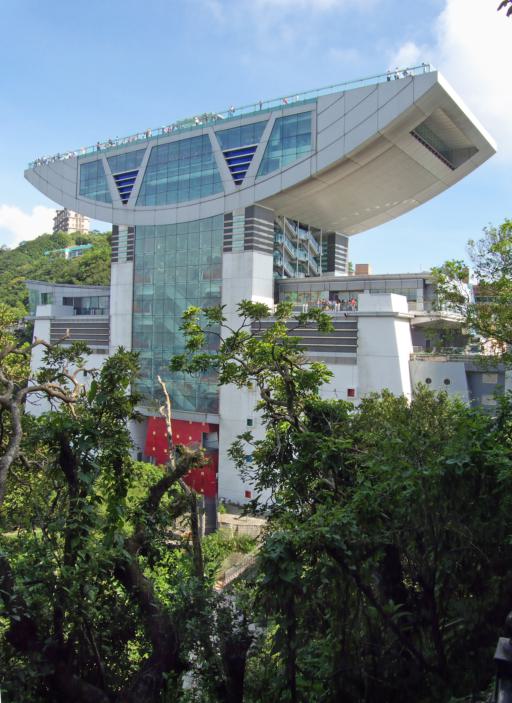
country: HK
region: Central and Western
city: Central
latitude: 22.2719
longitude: 114.1495
